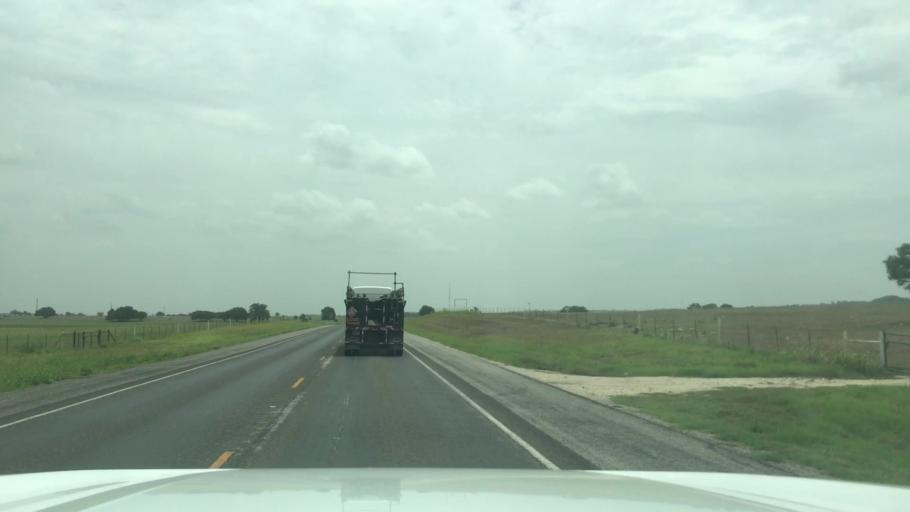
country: US
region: Texas
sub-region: Bosque County
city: Clifton
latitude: 31.8091
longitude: -97.6093
